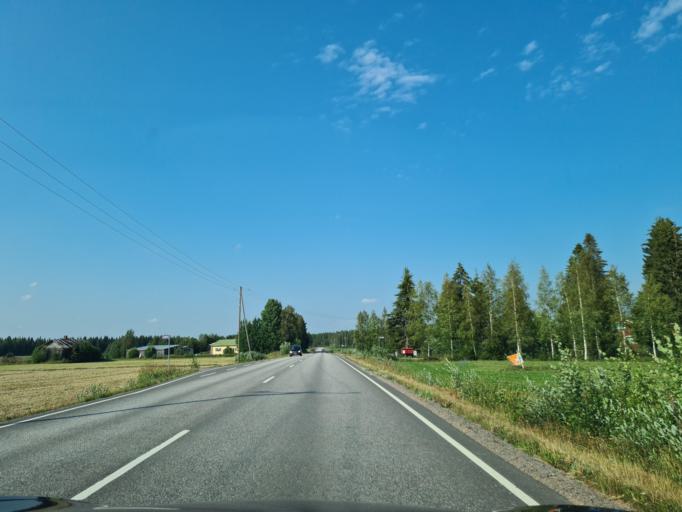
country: FI
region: Satakunta
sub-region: Pohjois-Satakunta
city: Kankaanpaeae
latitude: 61.9164
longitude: 22.5044
